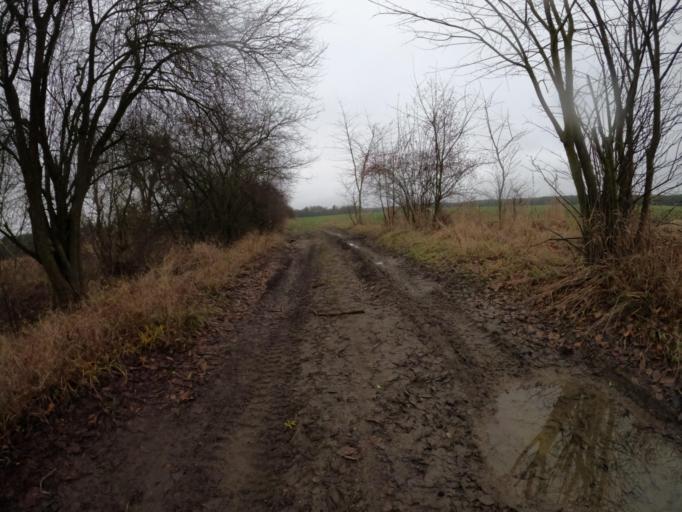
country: PL
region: West Pomeranian Voivodeship
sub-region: Powiat mysliborski
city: Debno
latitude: 52.7762
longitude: 14.7596
